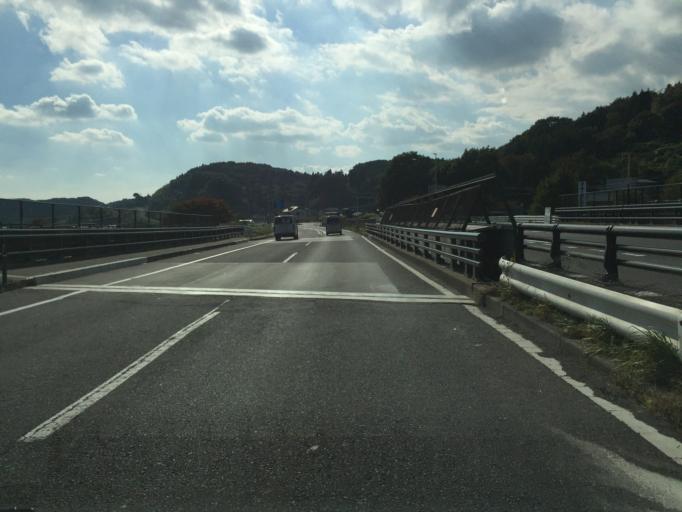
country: JP
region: Fukushima
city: Nihommatsu
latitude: 37.5705
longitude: 140.4162
